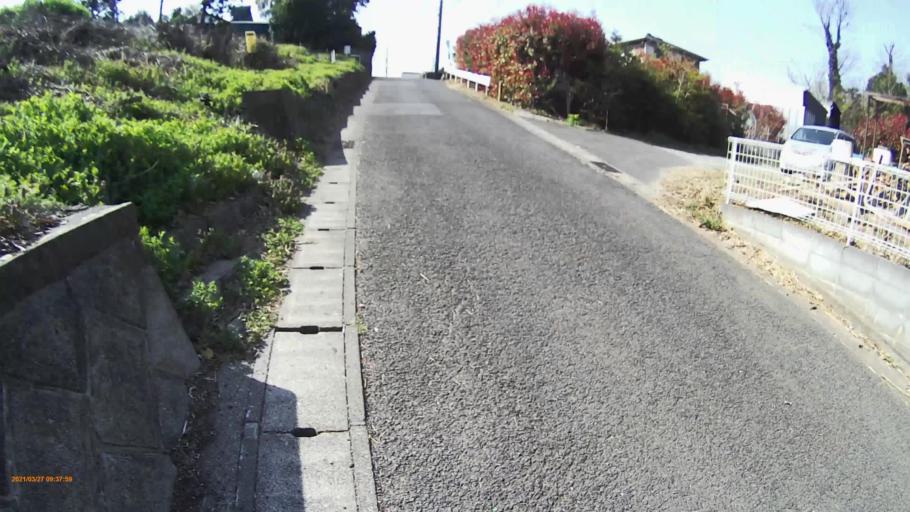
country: JP
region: Kanagawa
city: Atsugi
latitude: 35.4354
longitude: 139.4135
